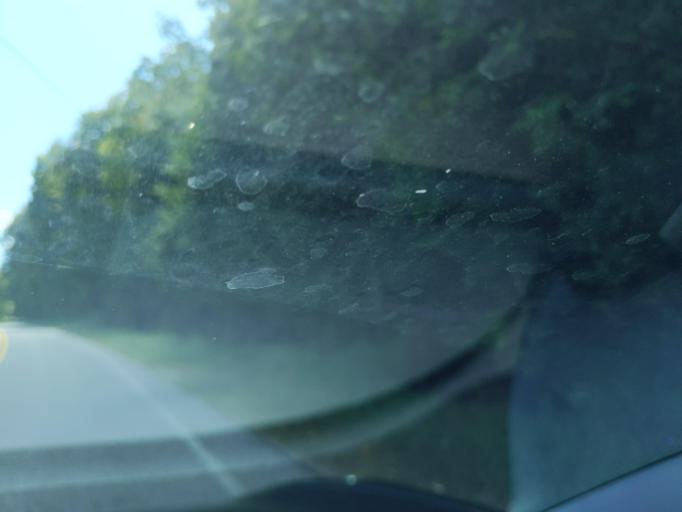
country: US
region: Michigan
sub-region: Antrim County
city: Elk Rapids
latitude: 44.9589
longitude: -85.3247
